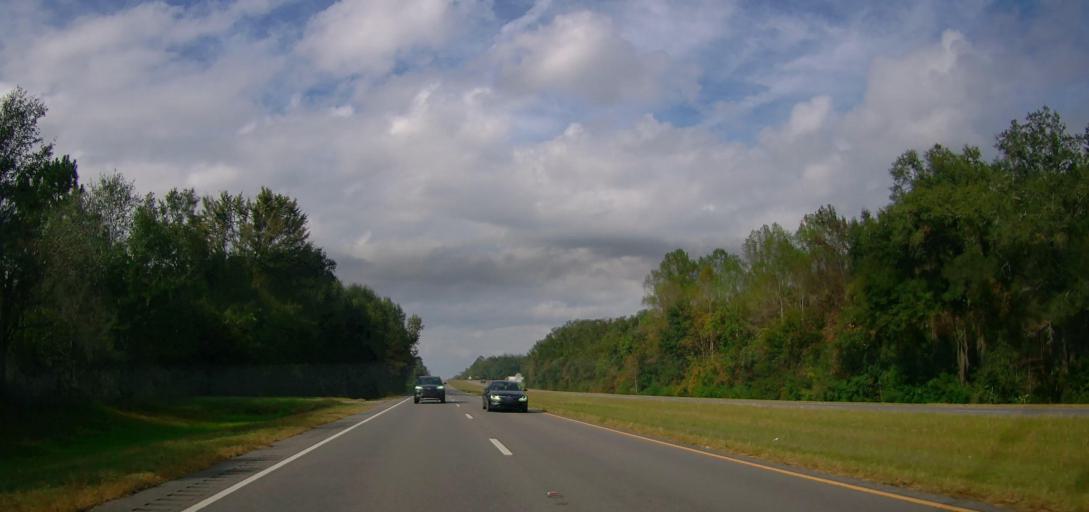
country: US
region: Georgia
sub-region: Thomas County
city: Meigs
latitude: 31.0047
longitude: -84.0502
